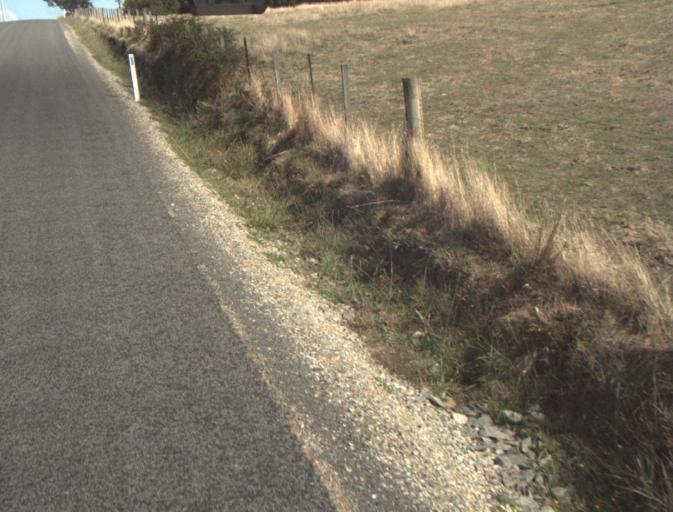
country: AU
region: Tasmania
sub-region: Launceston
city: Mayfield
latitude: -41.2317
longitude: 147.2353
